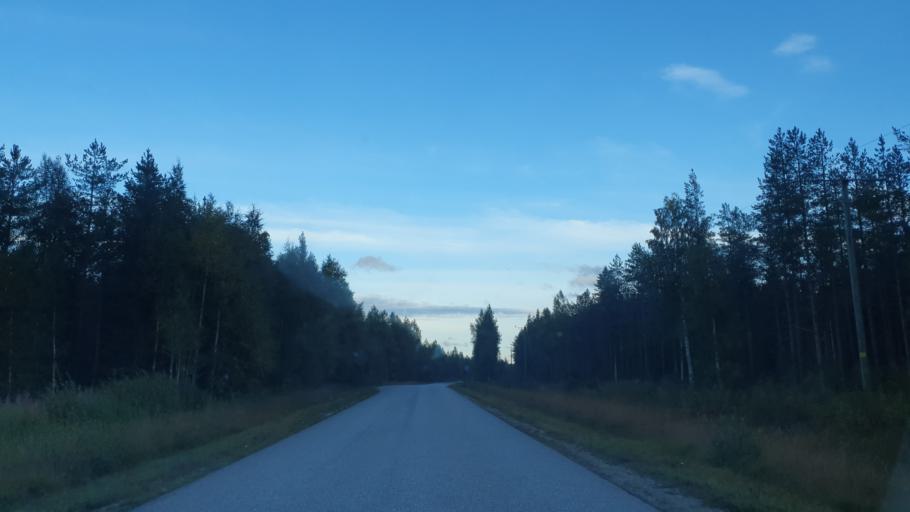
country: FI
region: Kainuu
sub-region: Kehys-Kainuu
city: Kuhmo
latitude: 64.4181
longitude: 29.9199
